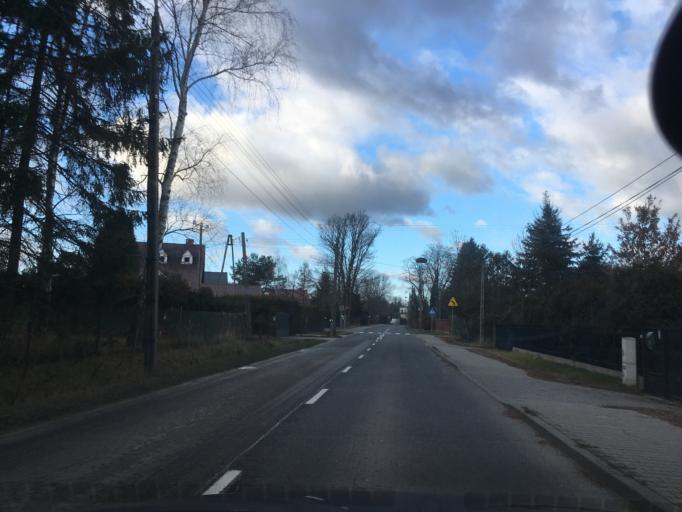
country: PL
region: Masovian Voivodeship
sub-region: Powiat piaseczynski
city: Lesznowola
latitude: 52.0350
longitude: 20.9483
